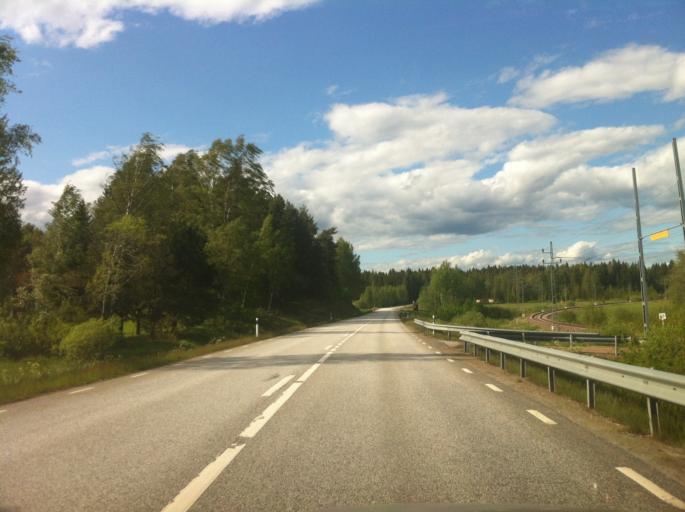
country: SE
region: Vaermland
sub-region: Storfors Kommun
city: Storfors
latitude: 59.4928
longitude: 14.2531
